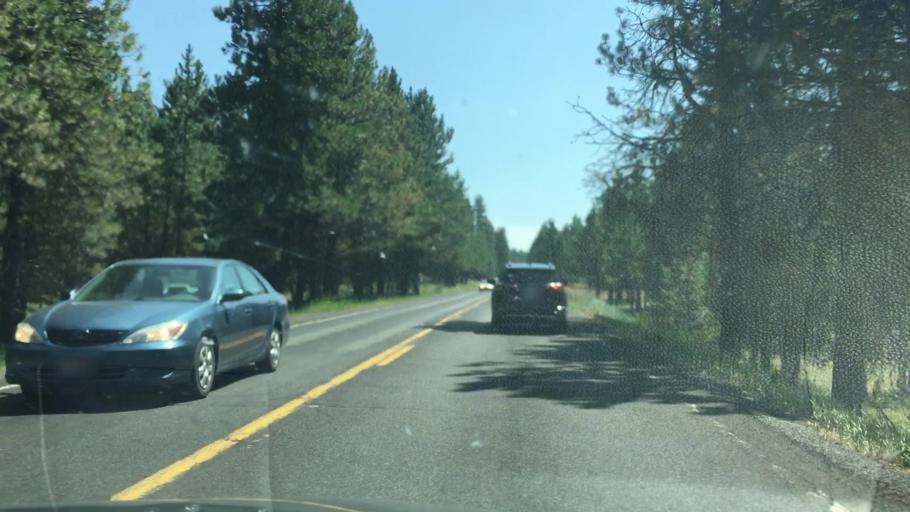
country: US
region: Idaho
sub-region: Valley County
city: McCall
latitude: 44.9404
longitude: -116.1667
